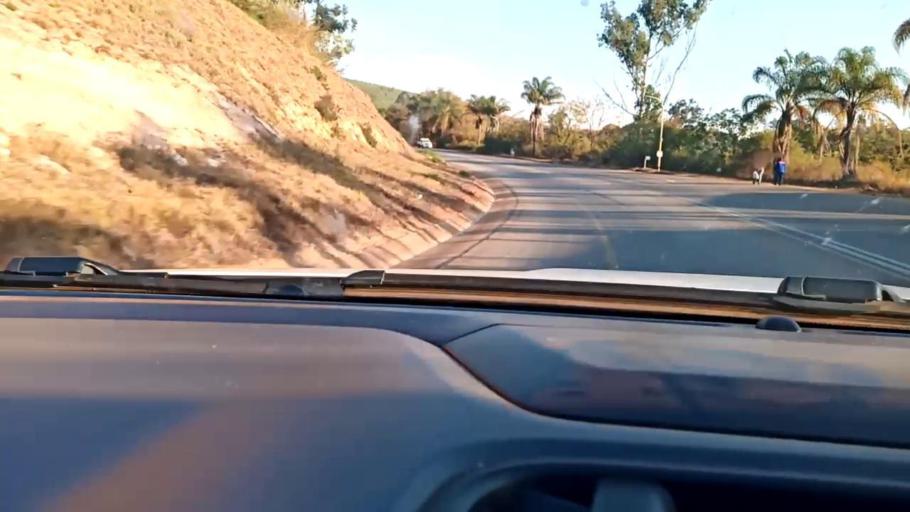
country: ZA
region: Limpopo
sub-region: Mopani District Municipality
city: Duiwelskloof
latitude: -23.6901
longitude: 30.1466
